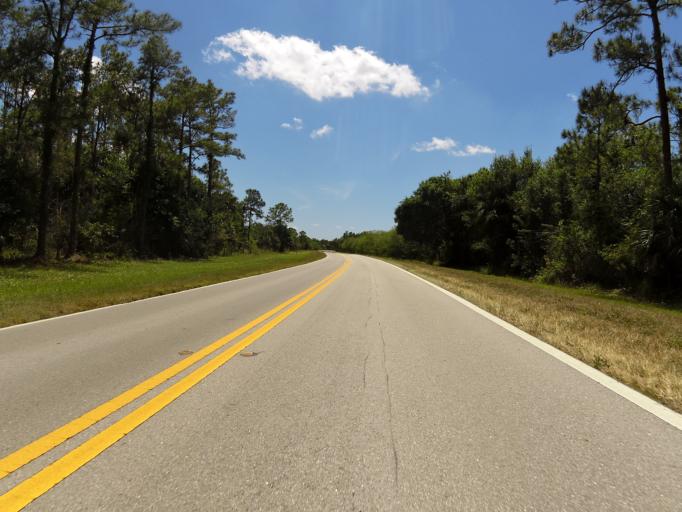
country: US
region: Florida
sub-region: Collier County
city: Immokalee
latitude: 26.3011
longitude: -81.3573
